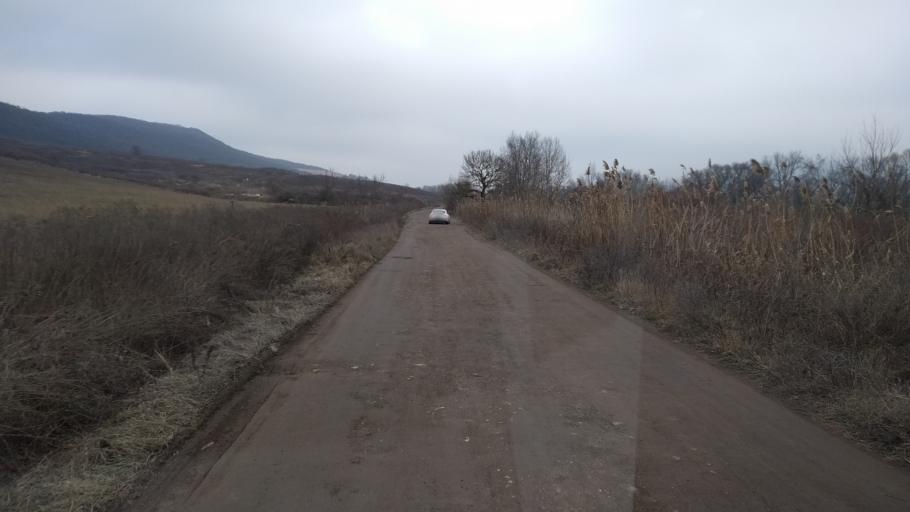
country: HU
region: Pest
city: Pilisborosjeno
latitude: 47.6045
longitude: 18.9649
